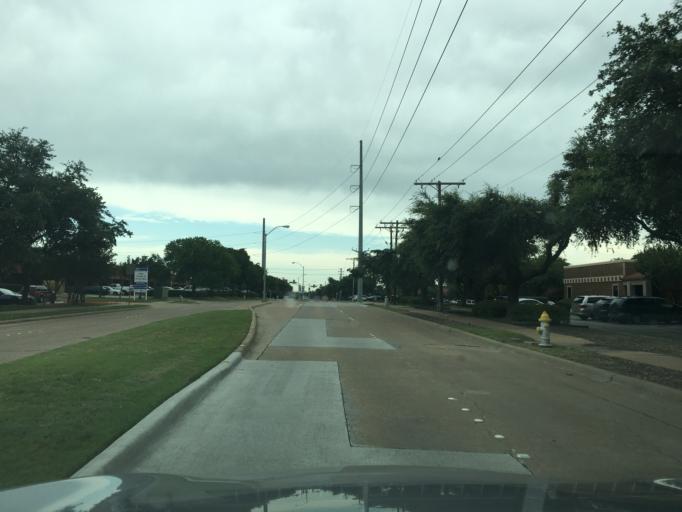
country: US
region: Texas
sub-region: Dallas County
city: Richardson
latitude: 32.9587
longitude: -96.7052
